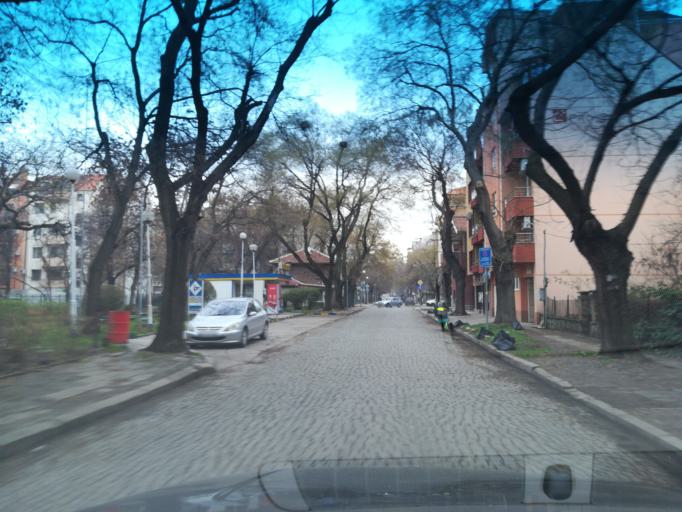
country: BG
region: Plovdiv
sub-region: Obshtina Plovdiv
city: Plovdiv
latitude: 42.1382
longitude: 24.7595
